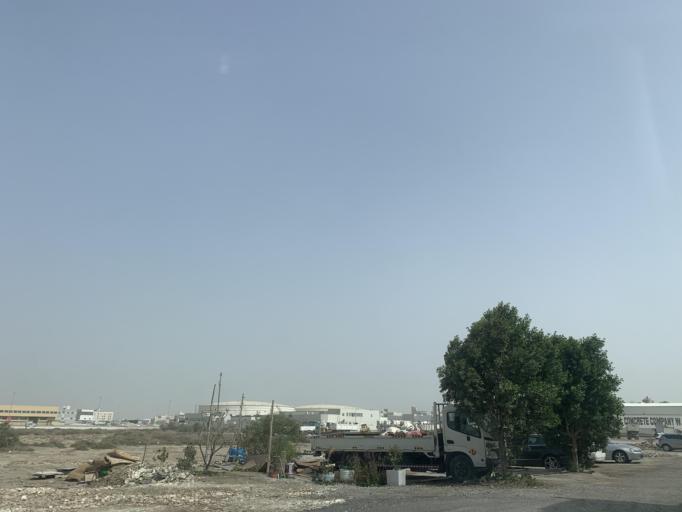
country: BH
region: Northern
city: Madinat `Isa
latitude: 26.1885
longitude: 50.5154
